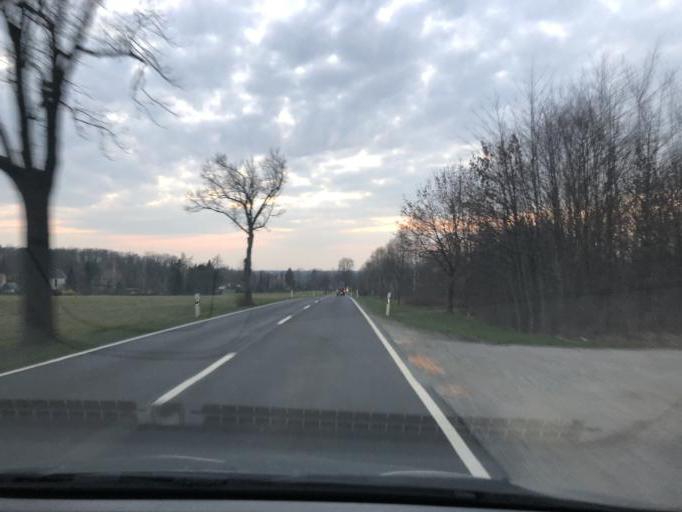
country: DE
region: Saxony
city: Konigsbruck
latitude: 51.2629
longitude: 13.9242
